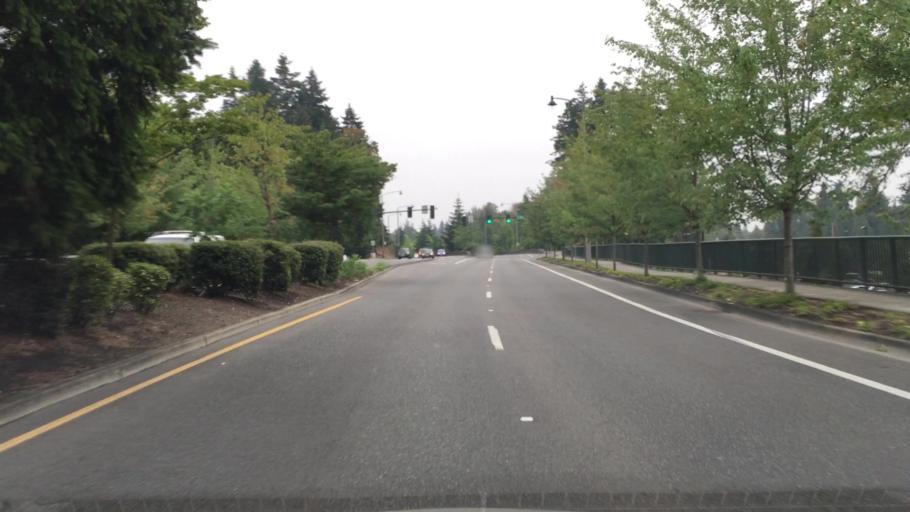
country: US
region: Washington
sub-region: King County
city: Newcastle
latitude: 47.5356
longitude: -122.1644
